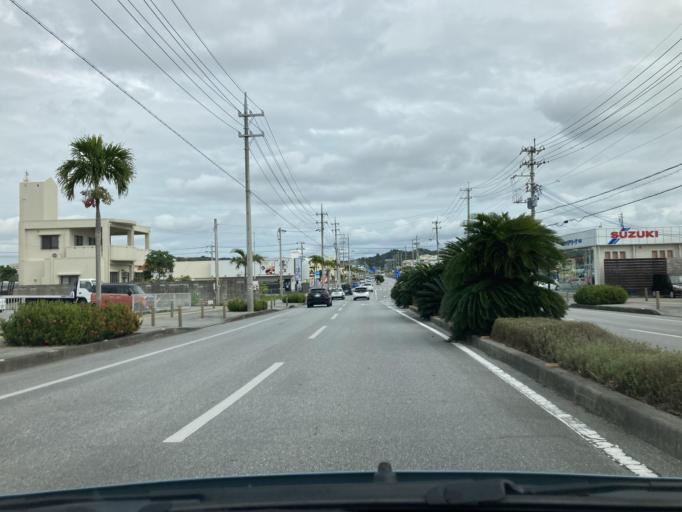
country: JP
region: Okinawa
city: Tomigusuku
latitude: 26.1606
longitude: 127.6622
